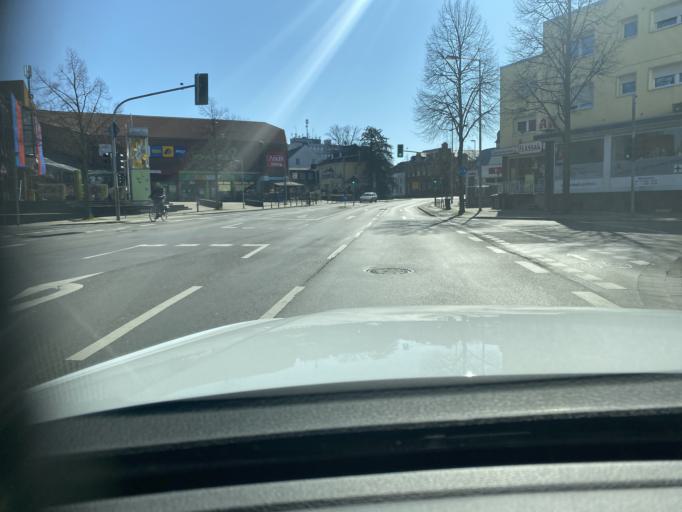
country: DE
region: North Rhine-Westphalia
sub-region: Regierungsbezirk Dusseldorf
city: Grevenbroich
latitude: 51.0887
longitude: 6.5923
